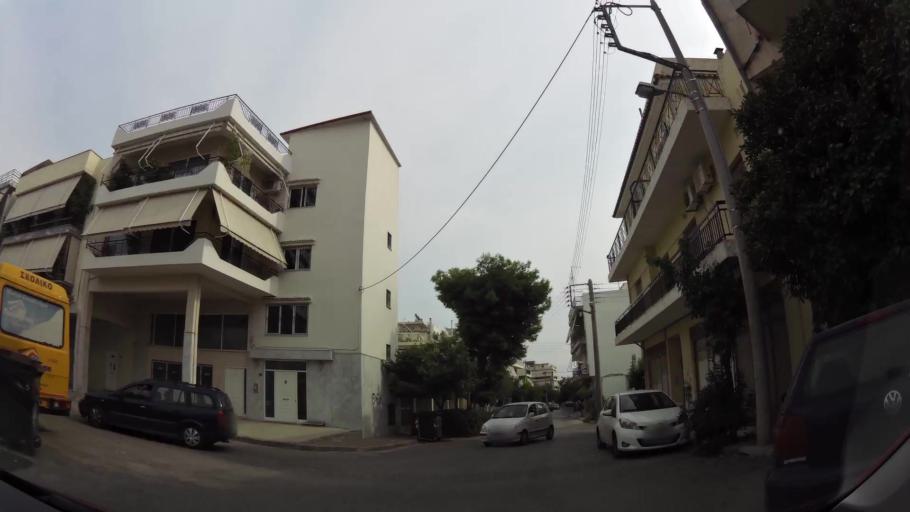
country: GR
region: Attica
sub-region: Nomarchia Athinas
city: Chaidari
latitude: 38.0091
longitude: 23.6769
